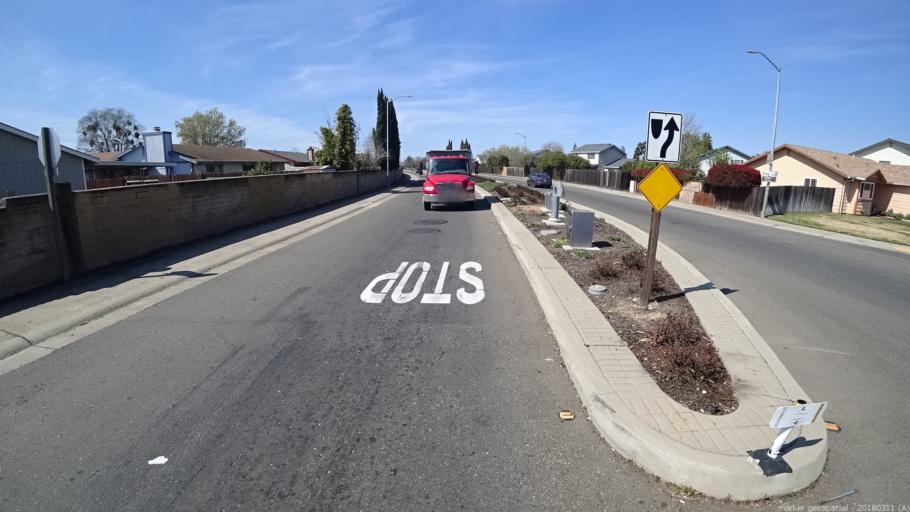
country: US
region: California
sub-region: Sacramento County
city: Florin
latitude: 38.4743
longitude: -121.4001
